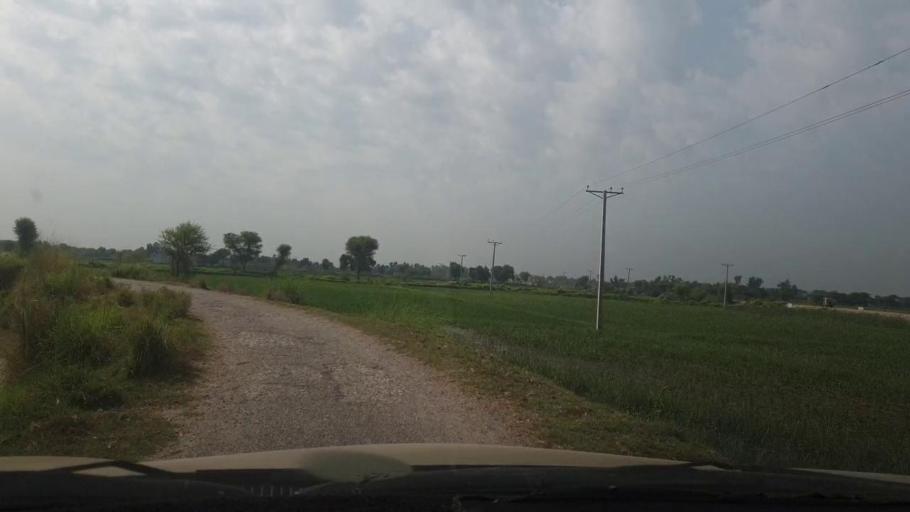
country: PK
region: Sindh
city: Larkana
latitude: 27.6420
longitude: 68.2021
